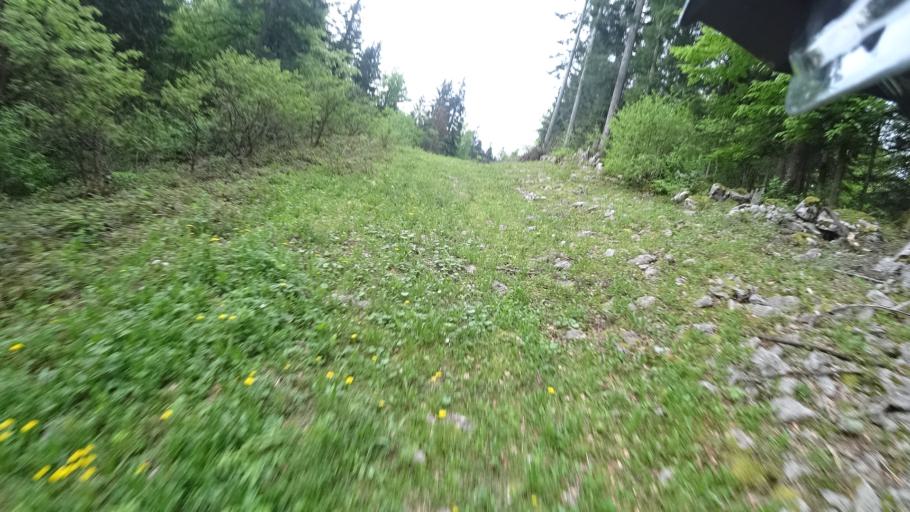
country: HR
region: Karlovacka
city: Plaski
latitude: 44.9575
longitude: 15.4136
